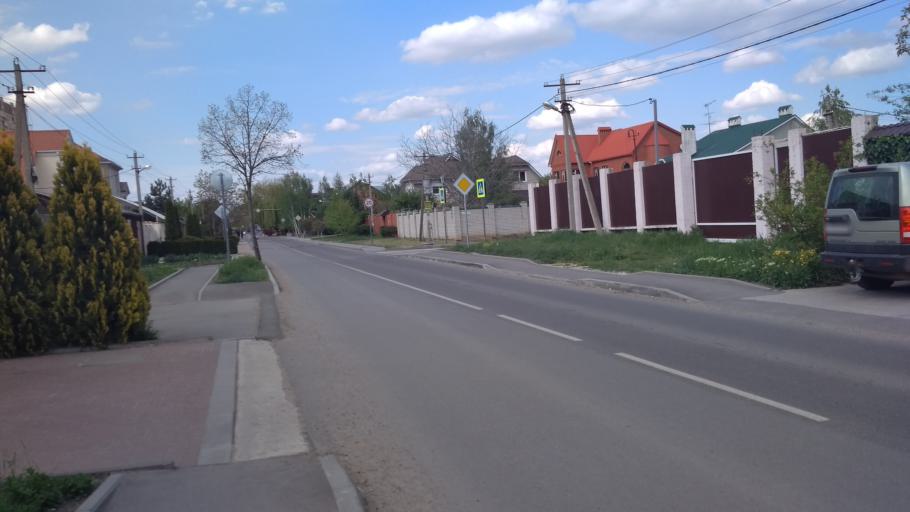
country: RU
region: Krasnodarskiy
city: Krasnodar
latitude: 45.0752
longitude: 39.0049
